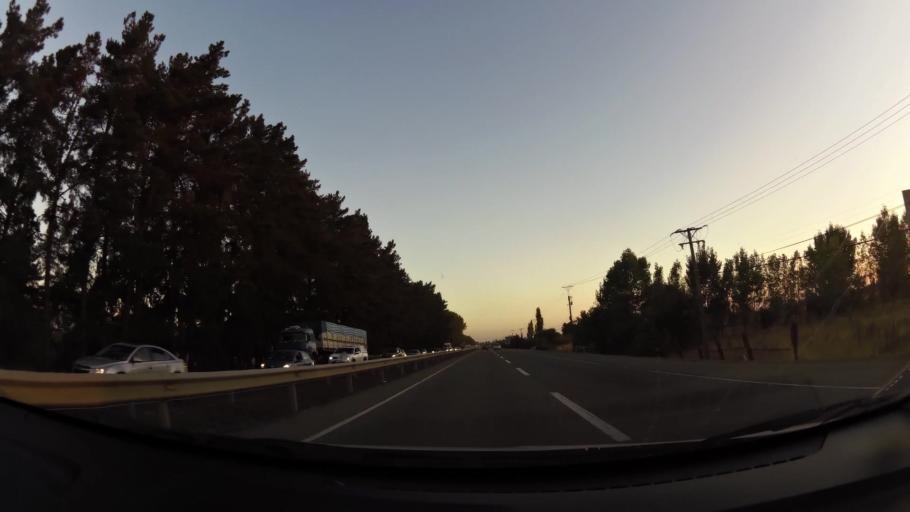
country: CL
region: Maule
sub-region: Provincia de Linares
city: Linares
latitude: -35.7514
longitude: -71.6733
